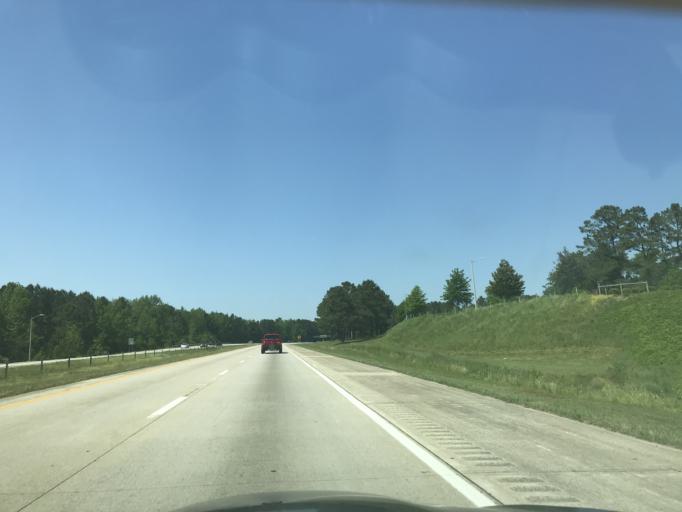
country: US
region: North Carolina
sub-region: Johnston County
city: Benson
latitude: 35.4378
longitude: -78.5337
